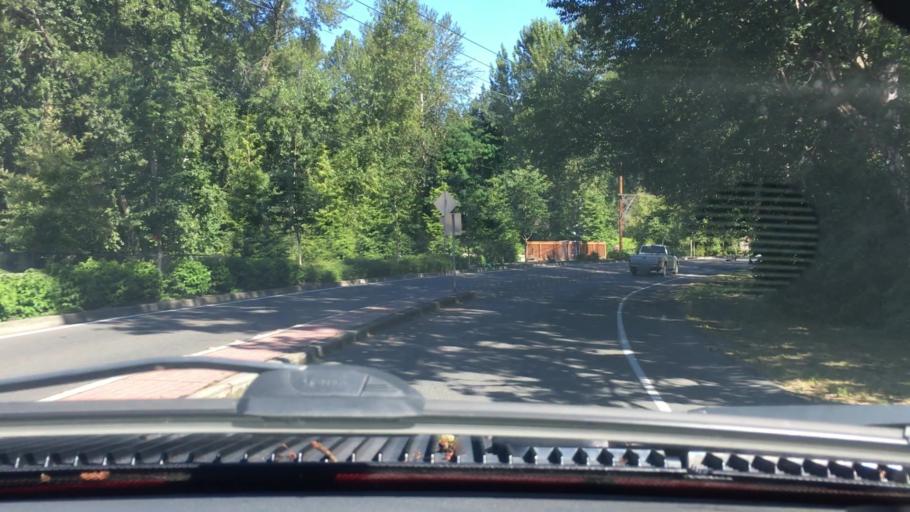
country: US
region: Washington
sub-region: King County
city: West Lake Sammamish
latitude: 47.5771
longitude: -122.1135
